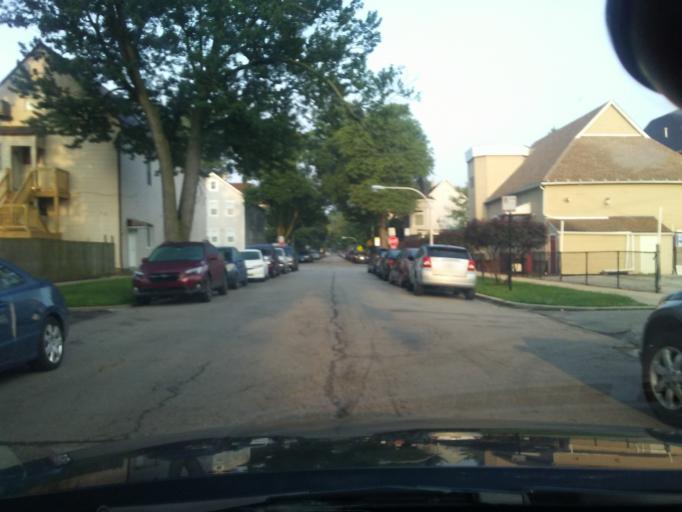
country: US
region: Illinois
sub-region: Cook County
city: Lincolnwood
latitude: 41.9522
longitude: -87.7037
